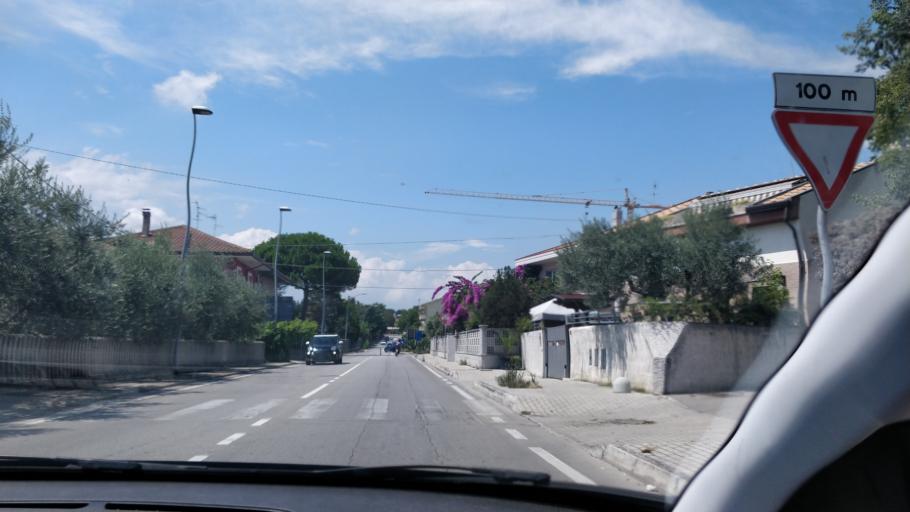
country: IT
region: Abruzzo
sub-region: Provincia di Chieti
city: Francavilla al Mare
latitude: 42.4243
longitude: 14.2749
